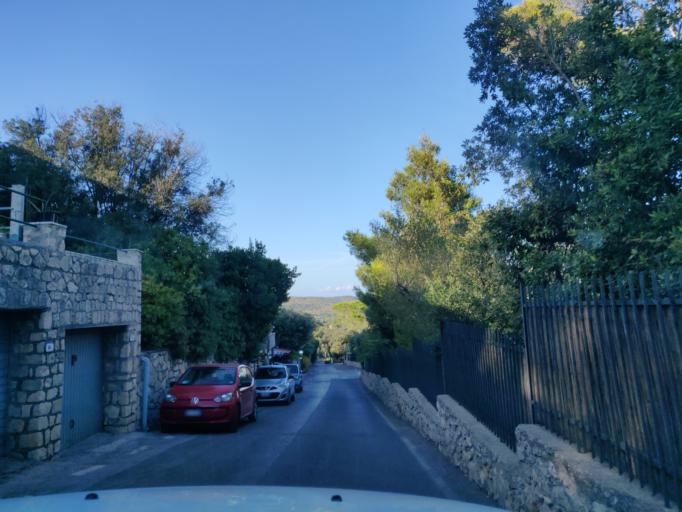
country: IT
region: Tuscany
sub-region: Provincia di Grosseto
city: Orbetello Scalo
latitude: 42.4081
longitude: 11.2907
